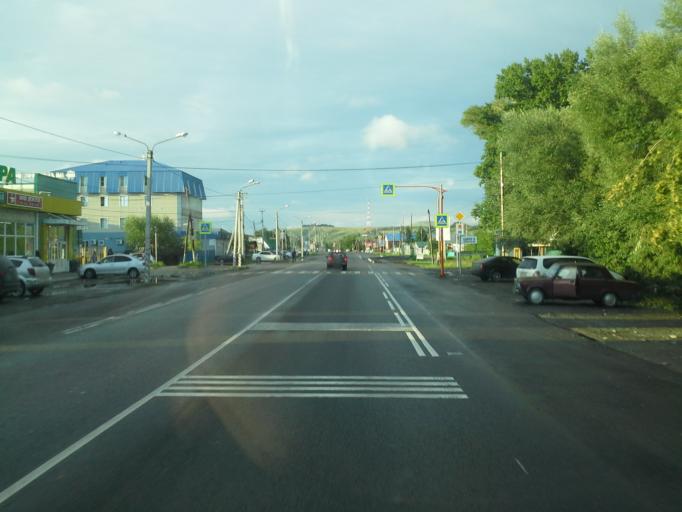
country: RU
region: Khabarovsk Krai
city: Mayma
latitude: 52.0119
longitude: 85.9129
